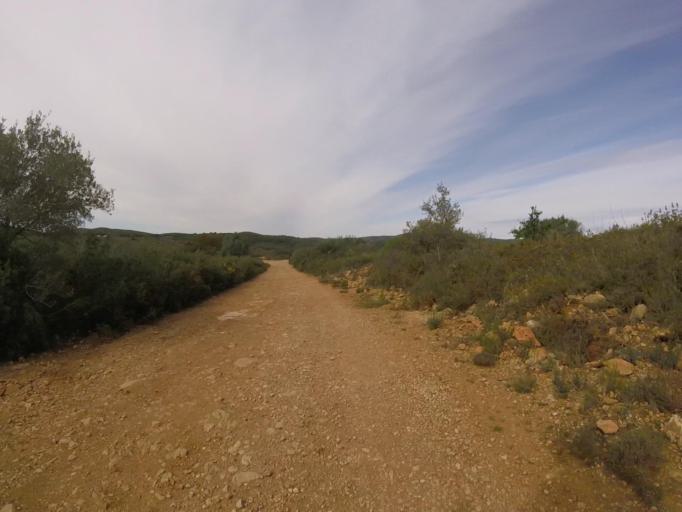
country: ES
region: Valencia
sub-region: Provincia de Castello
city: Torreblanca
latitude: 40.1972
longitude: 0.1334
